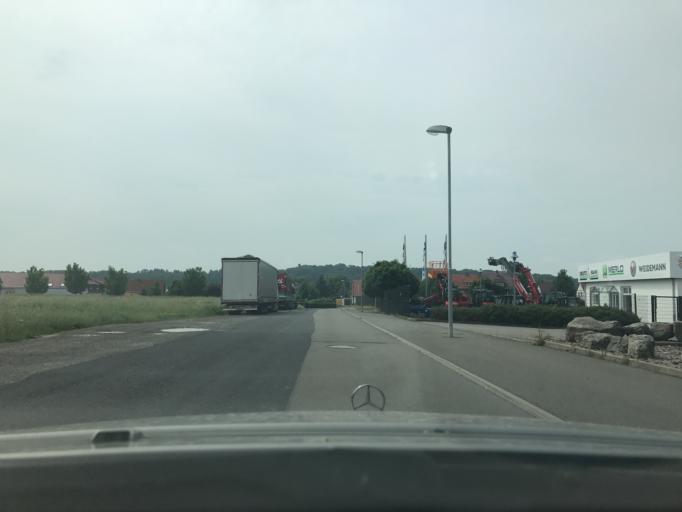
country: DE
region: Thuringia
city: Muehlhausen
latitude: 51.2149
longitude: 10.4918
